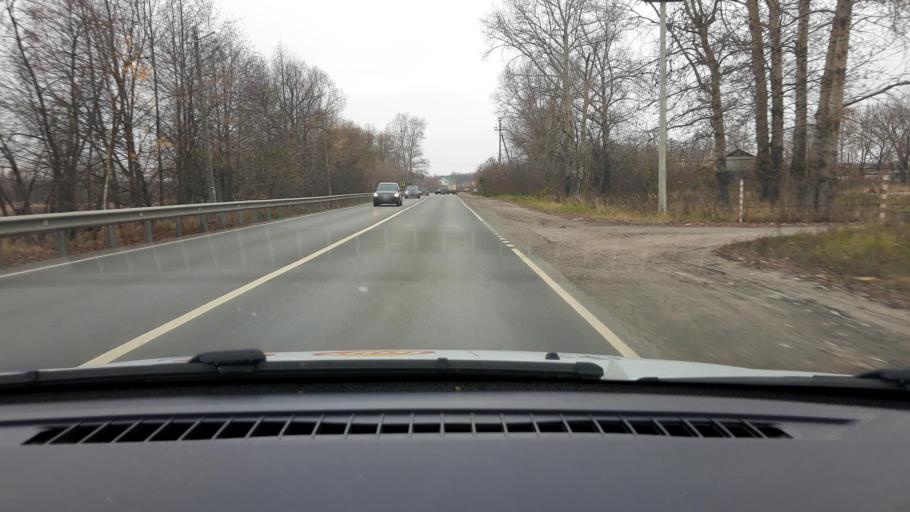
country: RU
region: Nizjnij Novgorod
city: Novaya Balakhna
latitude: 56.5072
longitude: 43.5878
